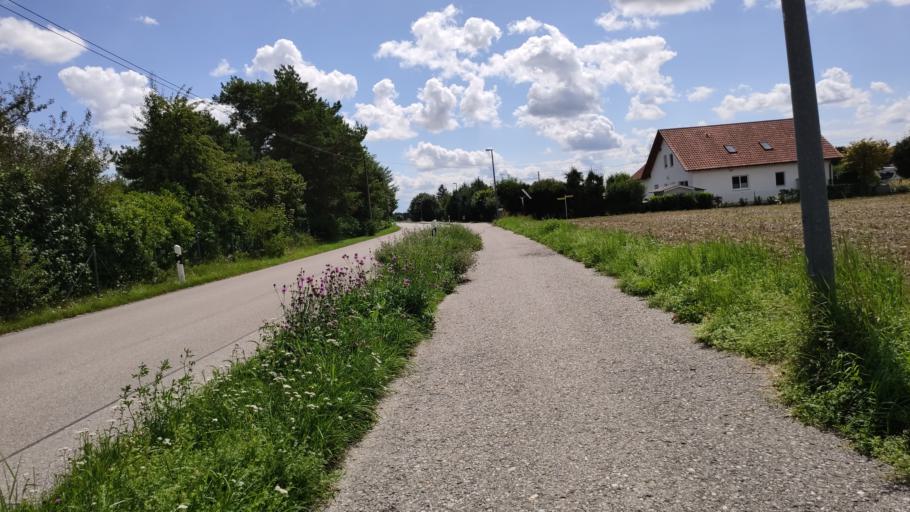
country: DE
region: Bavaria
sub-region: Swabia
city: Konigsbrunn
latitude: 48.2416
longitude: 10.8932
